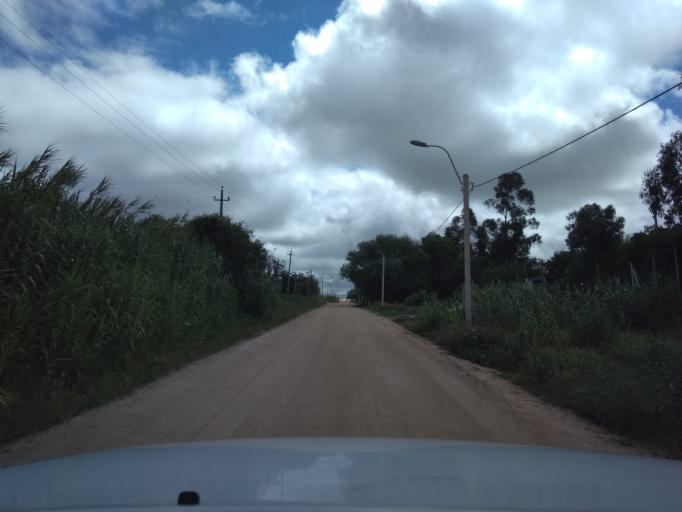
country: UY
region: Canelones
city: Pando
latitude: -34.6956
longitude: -55.9696
